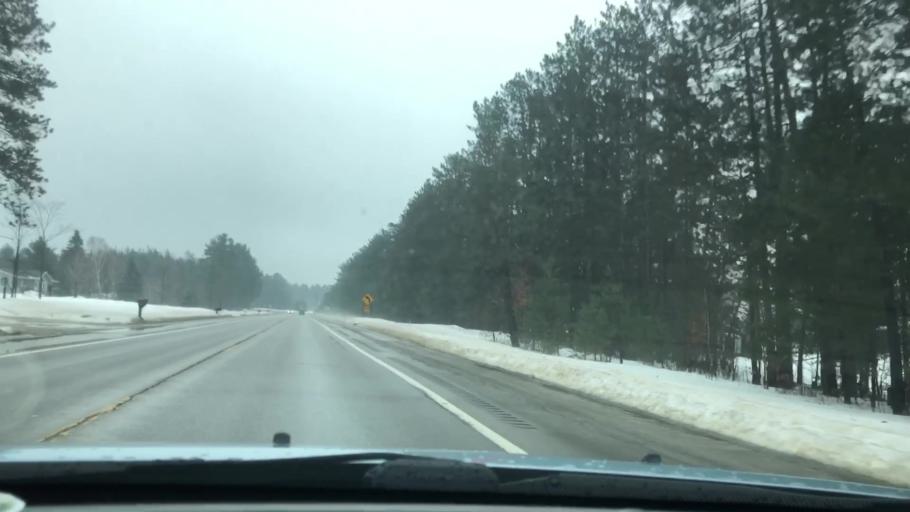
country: US
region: Michigan
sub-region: Otsego County
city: Gaylord
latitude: 45.0343
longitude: -84.7759
